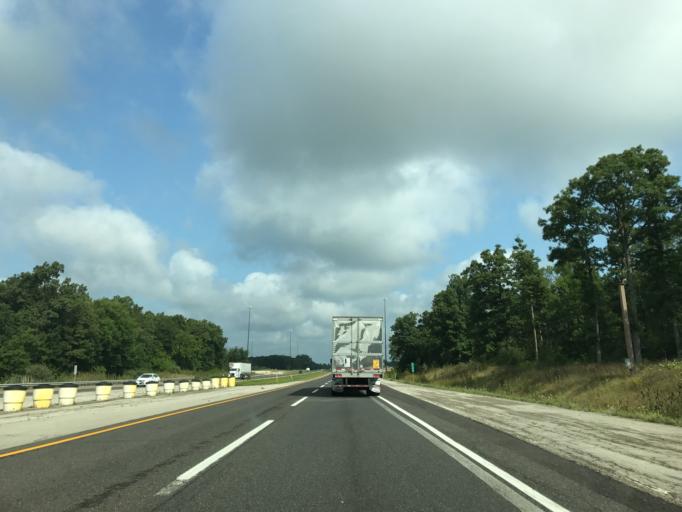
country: US
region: Indiana
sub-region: Steuben County
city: Fremont
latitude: 41.7219
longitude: -84.9628
